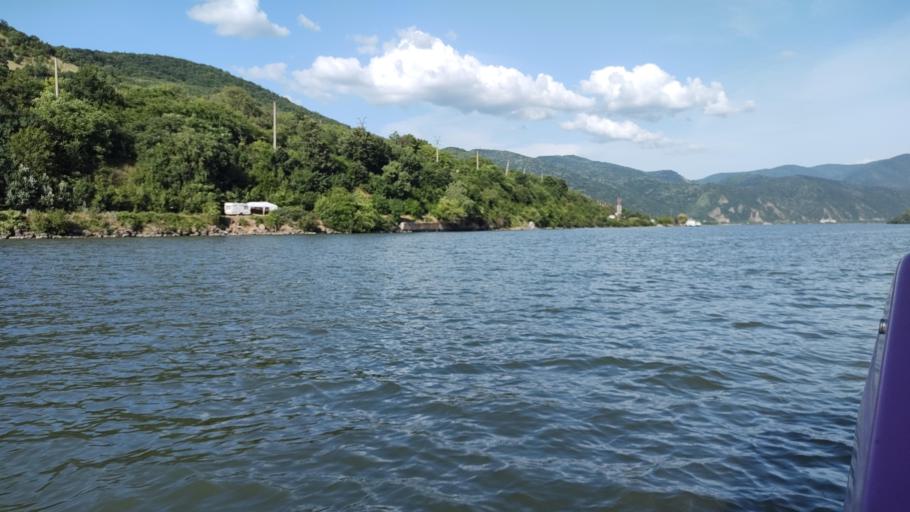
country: RO
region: Caras-Severin
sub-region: Comuna Berzasca
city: Berzasca
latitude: 44.6374
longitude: 21.9572
